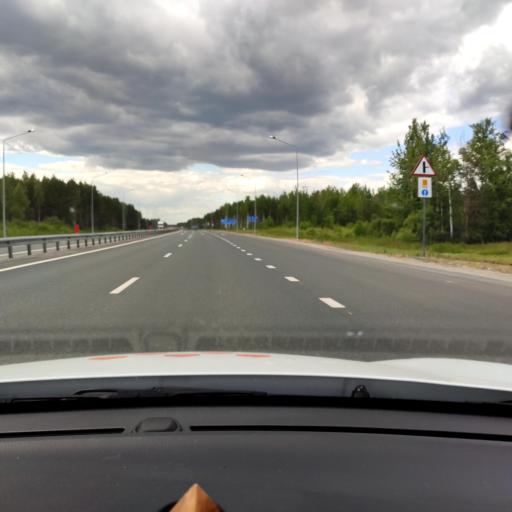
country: RU
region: Mariy-El
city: Surok
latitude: 56.4452
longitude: 48.1070
